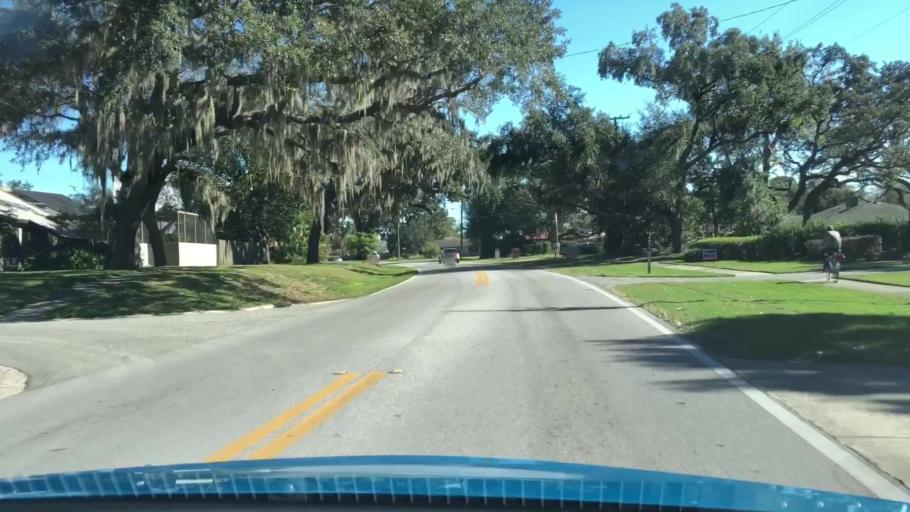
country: US
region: Florida
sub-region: Orange County
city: Pine Castle
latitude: 28.4807
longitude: -81.3452
